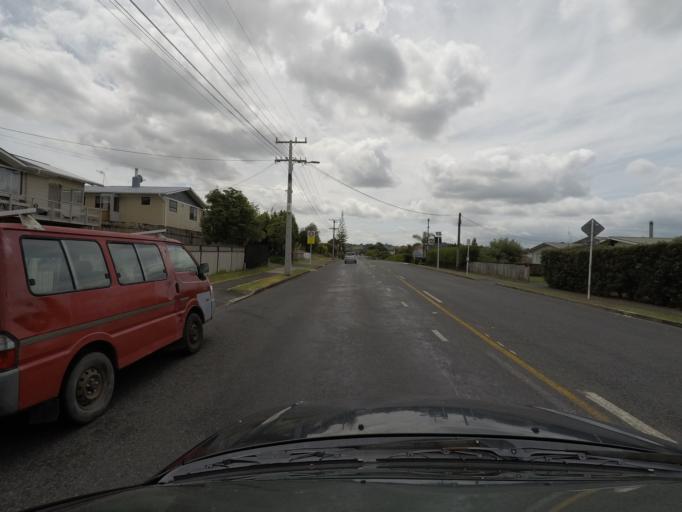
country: NZ
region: Northland
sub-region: Whangarei
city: Whangarei
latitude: -35.6834
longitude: 174.3271
